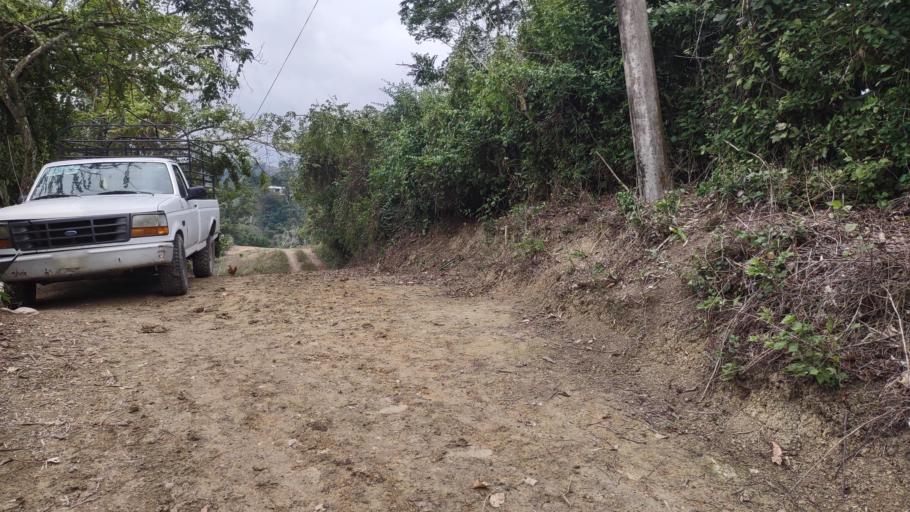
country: MX
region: Veracruz
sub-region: Coatzintla
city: Manuel Maria Contreras
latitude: 20.4110
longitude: -97.4586
